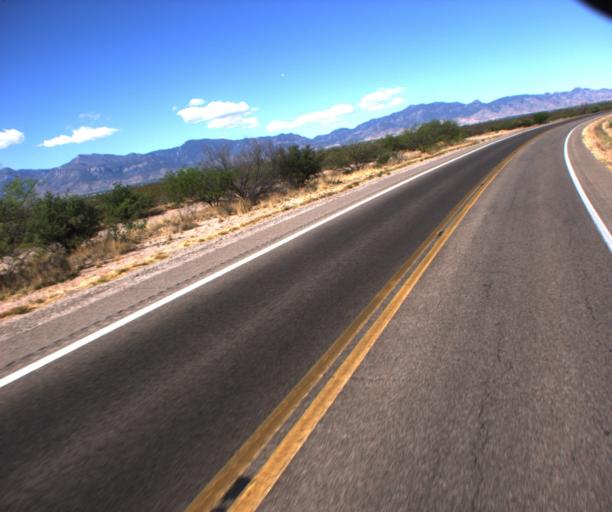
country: US
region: Arizona
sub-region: Cochise County
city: Sierra Vista Southeast
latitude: 31.5463
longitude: -110.1561
